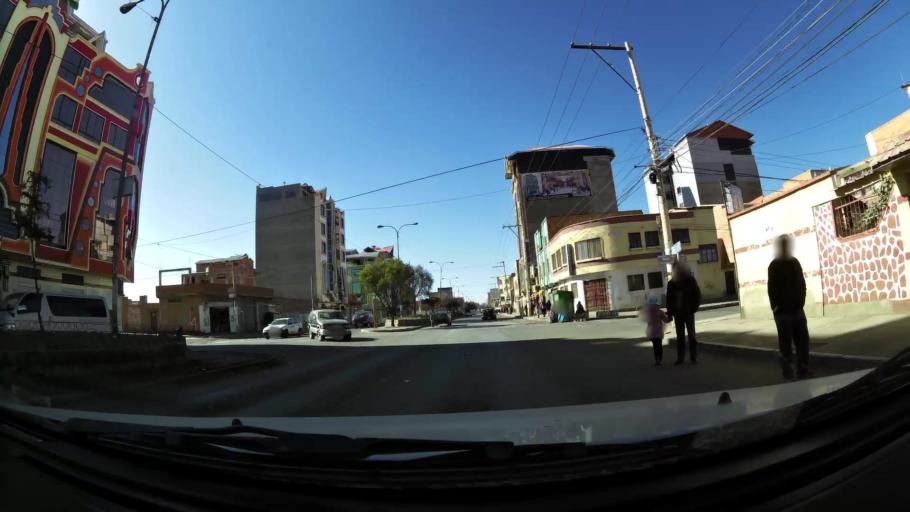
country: BO
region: La Paz
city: La Paz
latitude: -16.5214
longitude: -68.2049
